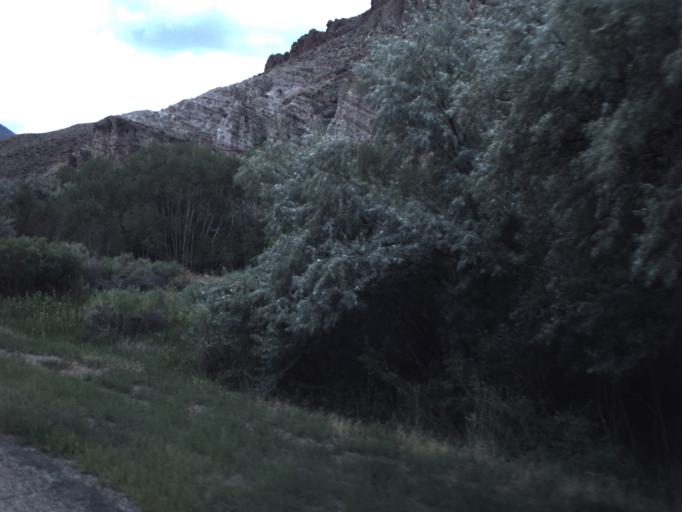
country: US
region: Utah
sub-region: Piute County
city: Junction
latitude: 38.2043
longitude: -112.1794
